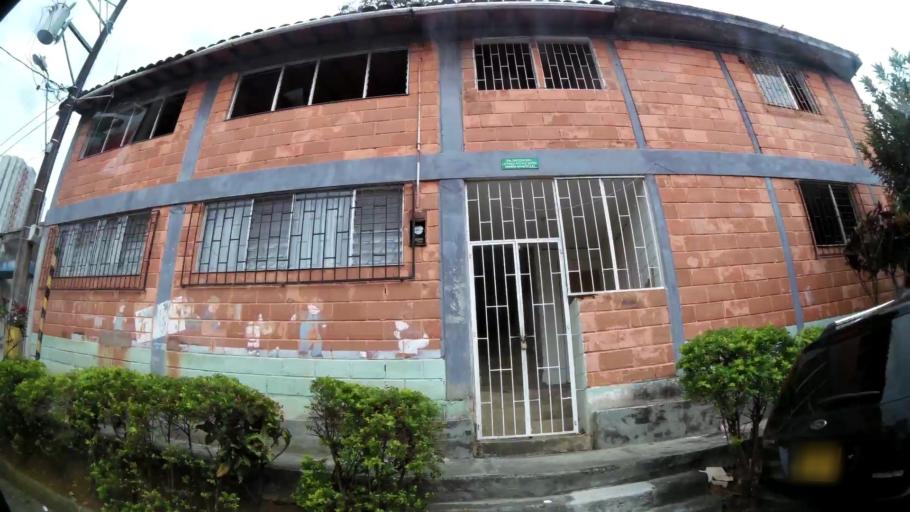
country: CO
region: Antioquia
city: Medellin
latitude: 6.2810
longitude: -75.5978
